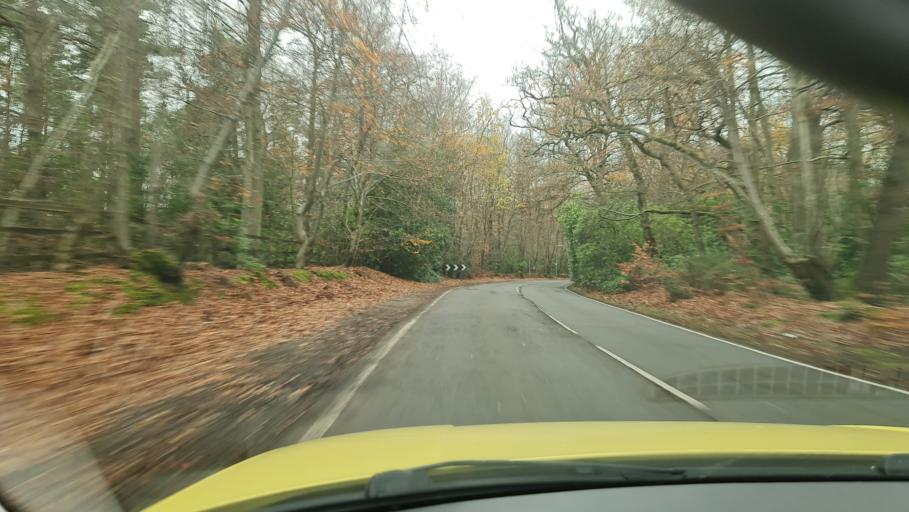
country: GB
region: England
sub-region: Bracknell Forest
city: Sandhurst
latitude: 51.3203
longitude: -0.7811
